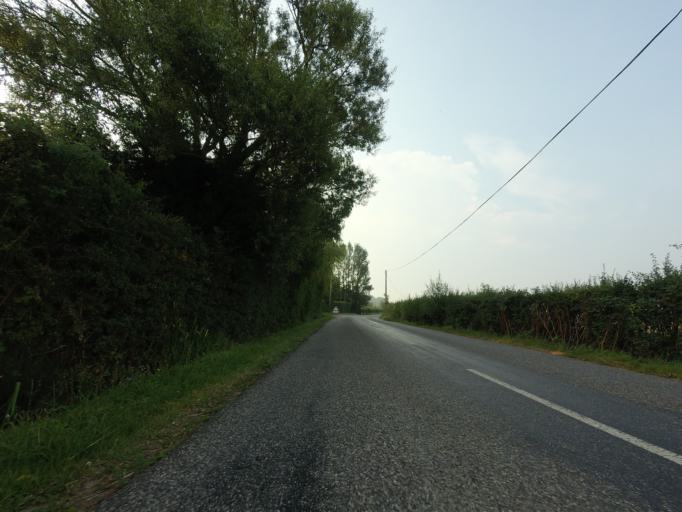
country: GB
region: England
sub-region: Kent
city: Ashford
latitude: 51.1301
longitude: 0.8200
